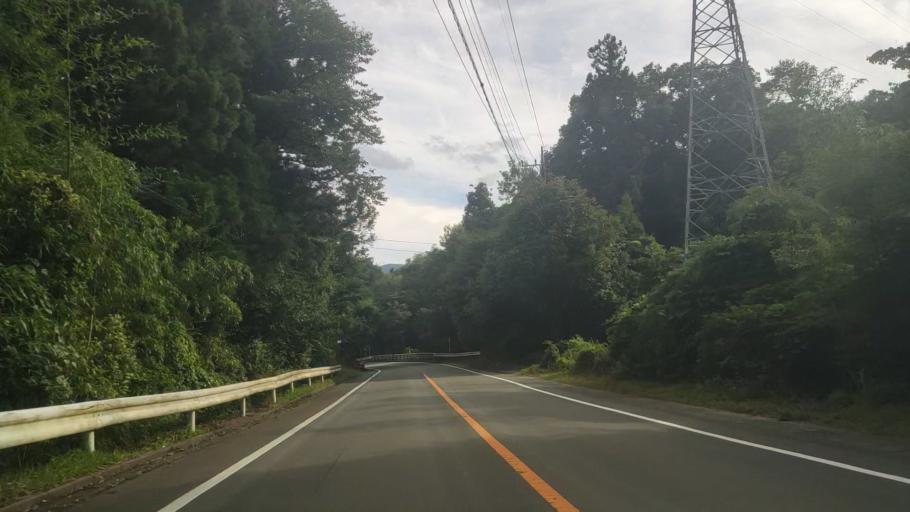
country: JP
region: Gunma
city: Kiryu
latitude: 36.5967
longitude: 139.4036
